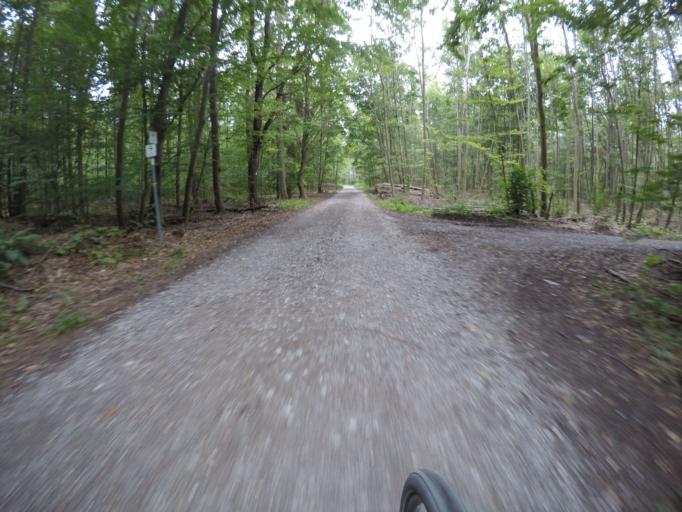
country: DE
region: Baden-Wuerttemberg
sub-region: Regierungsbezirk Stuttgart
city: Eberdingen
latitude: 48.8720
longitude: 8.9903
